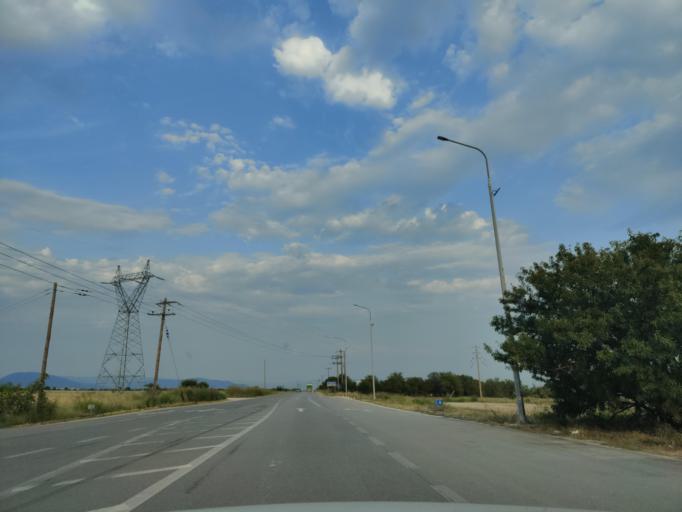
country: GR
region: East Macedonia and Thrace
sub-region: Nomos Dramas
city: Petroussa
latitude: 41.1772
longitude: 24.0028
